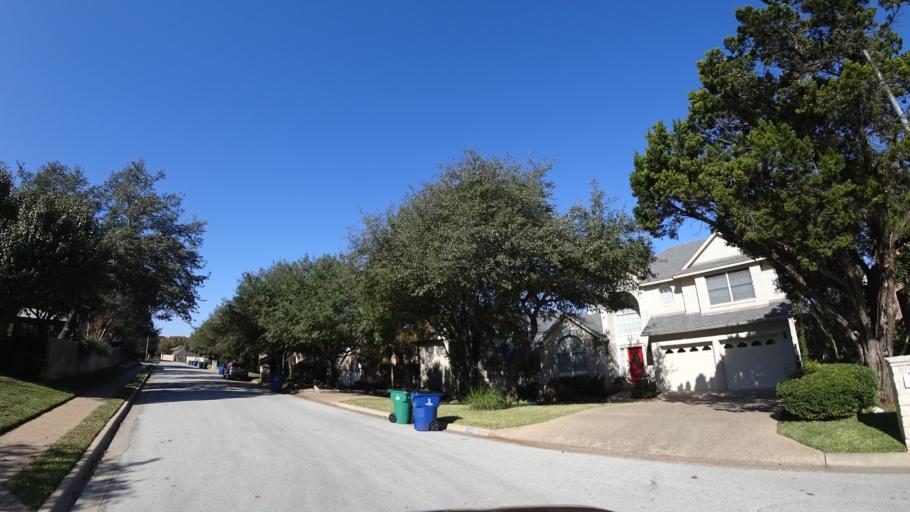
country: US
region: Texas
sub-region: Travis County
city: Lost Creek
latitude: 30.3772
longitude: -97.8463
